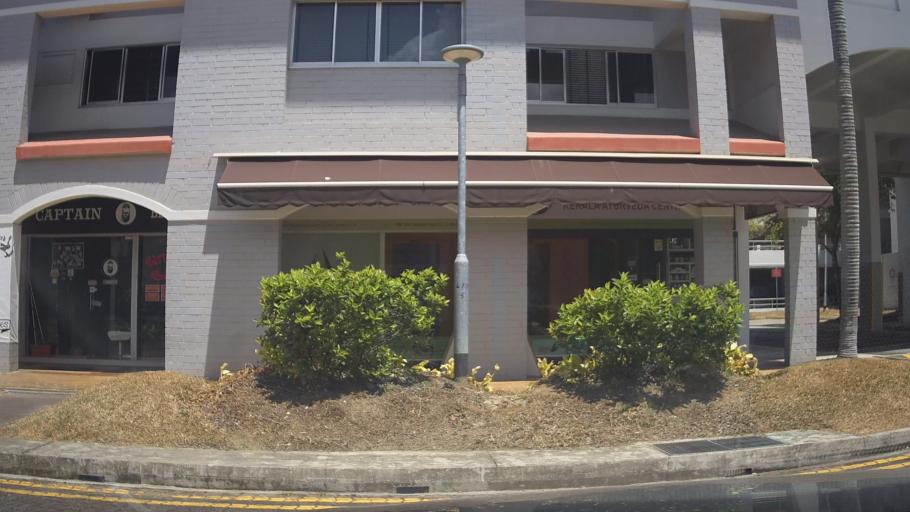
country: SG
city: Singapore
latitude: 1.3597
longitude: 103.9534
